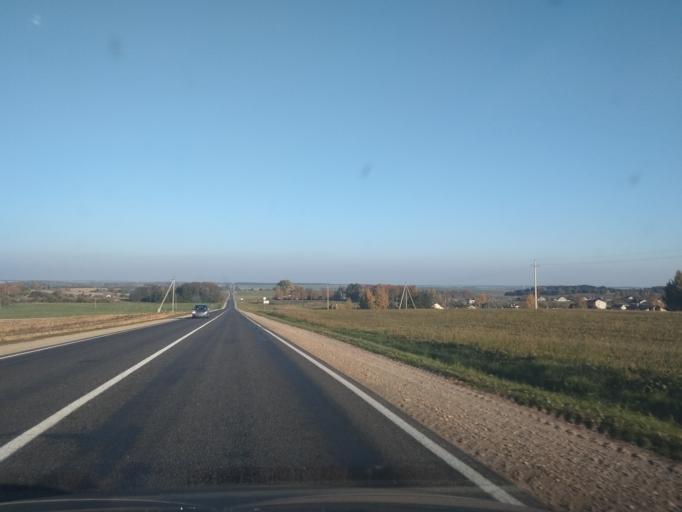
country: BY
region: Grodnenskaya
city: Svislach
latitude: 53.1315
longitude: 24.1899
